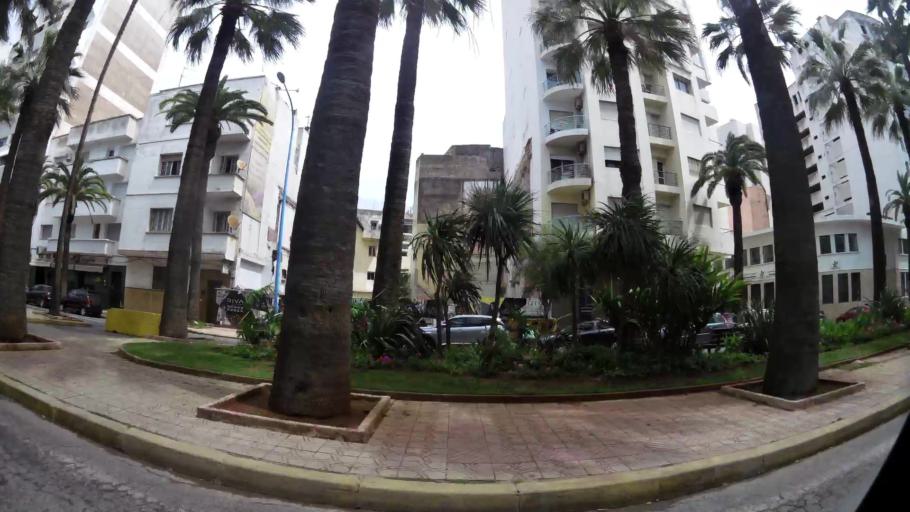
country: MA
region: Grand Casablanca
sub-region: Casablanca
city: Casablanca
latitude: 33.5948
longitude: -7.6298
